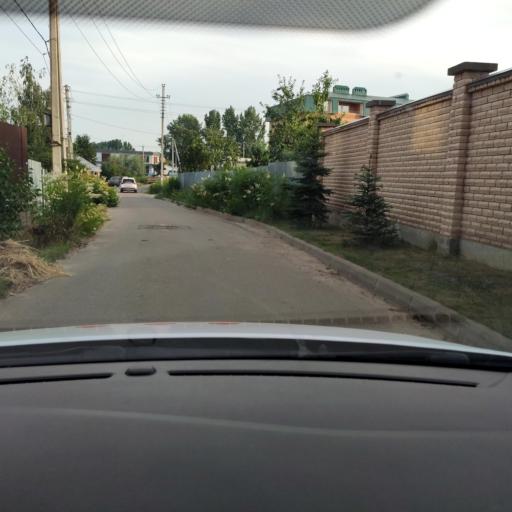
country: RU
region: Tatarstan
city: Stolbishchi
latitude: 55.7510
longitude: 49.2544
